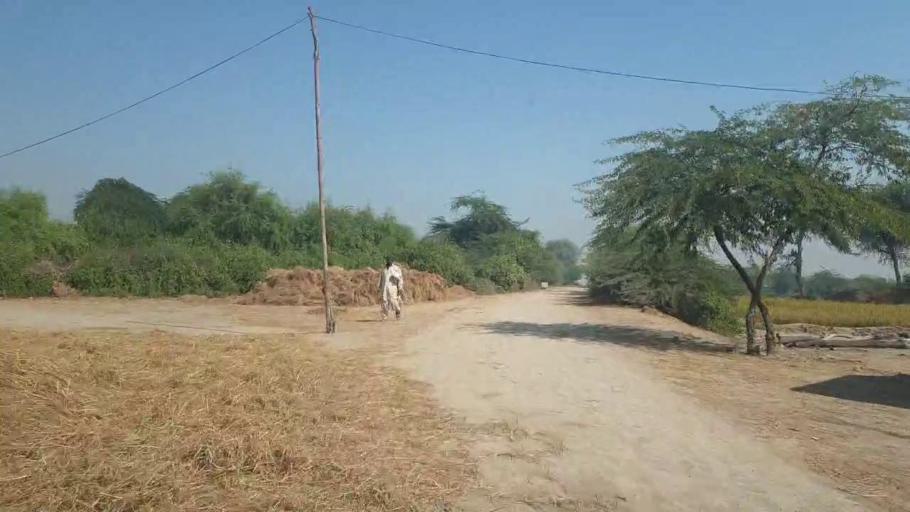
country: PK
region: Sindh
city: Badin
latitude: 24.6769
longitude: 68.8578
